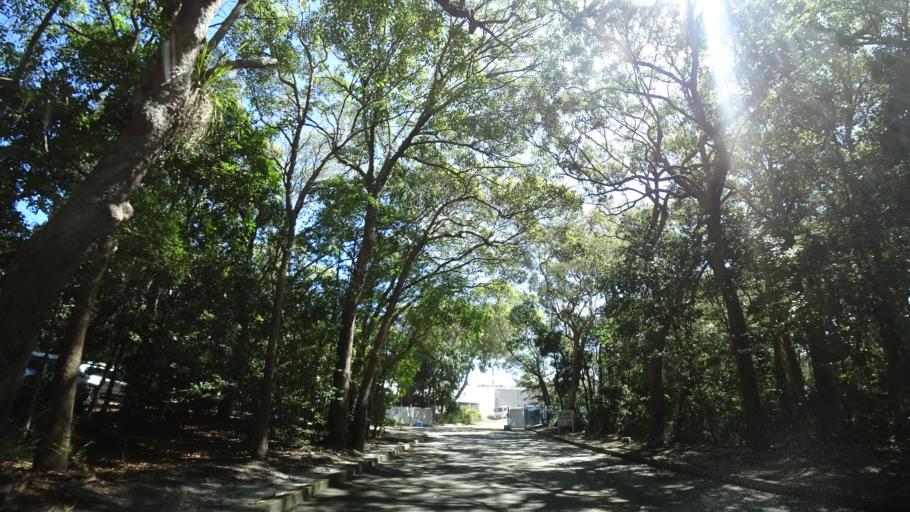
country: AU
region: Queensland
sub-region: Sunshine Coast
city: Mooloolaba
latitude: -26.6325
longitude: 153.0959
